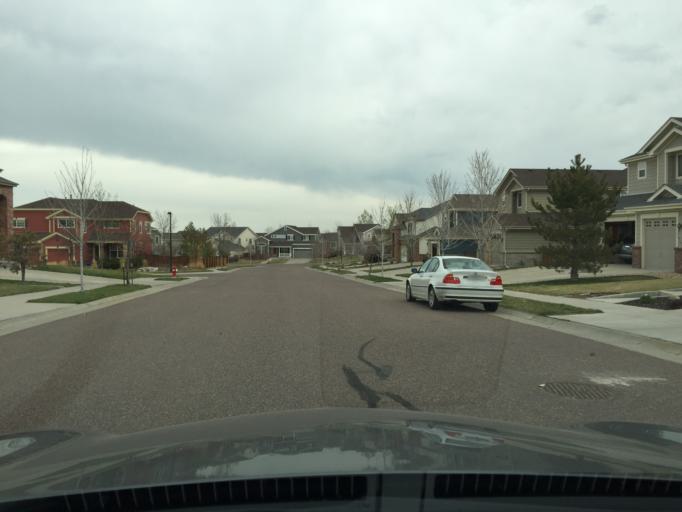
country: US
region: Colorado
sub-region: Boulder County
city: Erie
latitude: 40.0089
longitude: -105.0181
